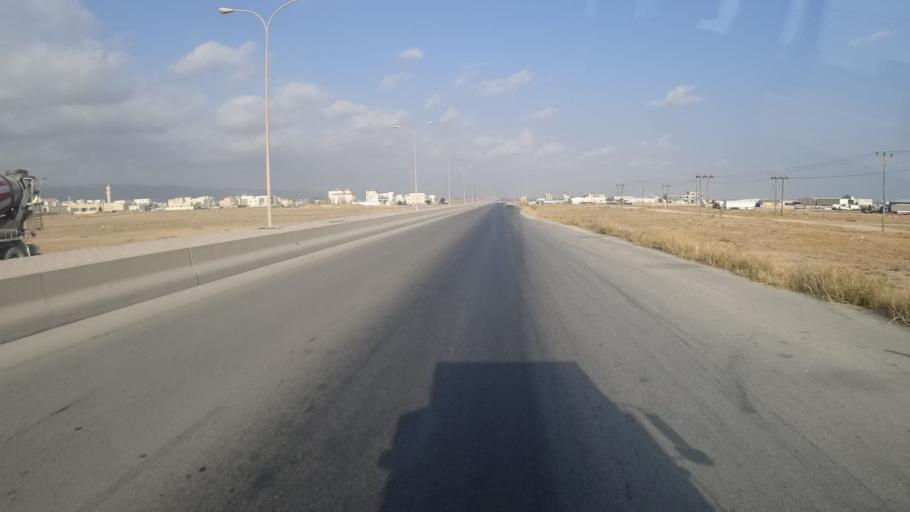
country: OM
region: Zufar
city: Salalah
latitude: 17.0363
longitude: 54.0392
